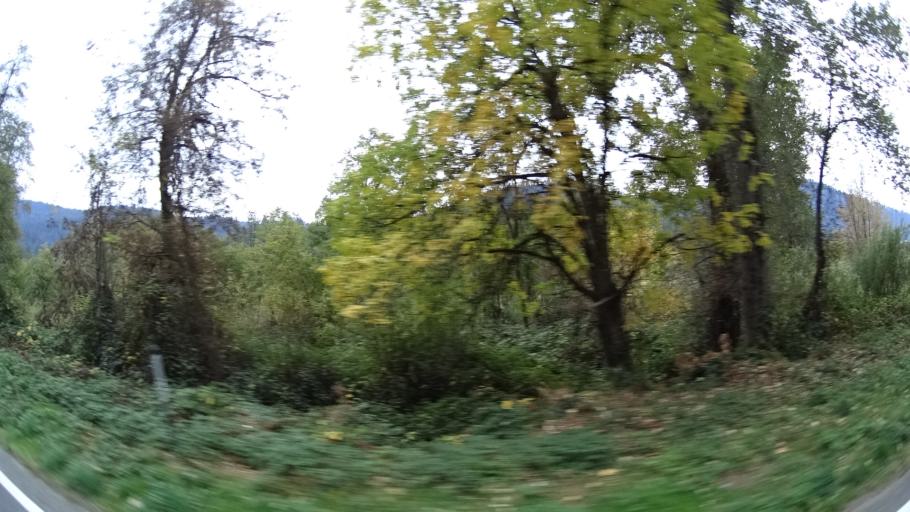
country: US
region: California
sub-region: Siskiyou County
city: Happy Camp
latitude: 41.8094
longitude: -123.3629
